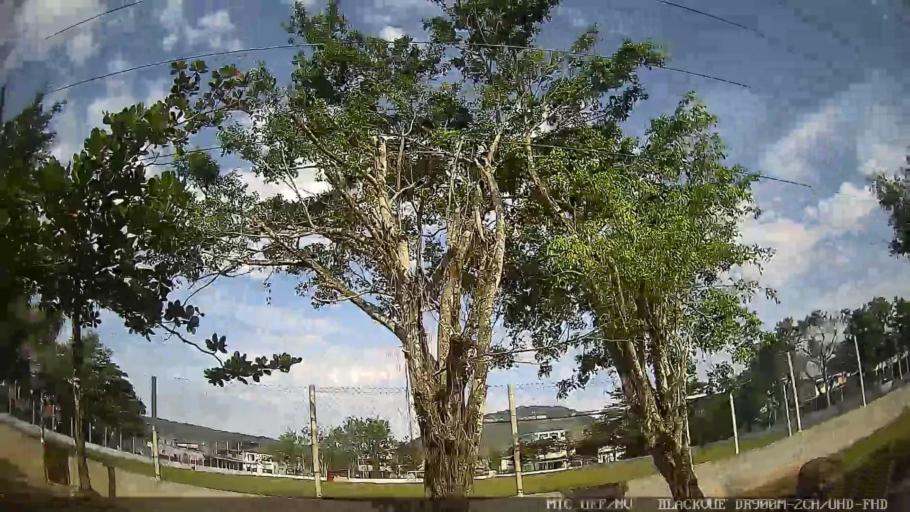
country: BR
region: Sao Paulo
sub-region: Guaruja
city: Guaruja
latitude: -23.9625
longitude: -46.2586
